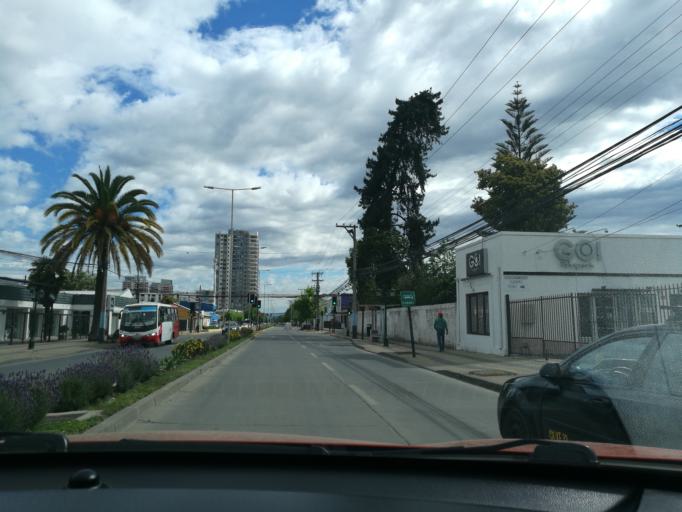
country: CL
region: O'Higgins
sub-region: Provincia de Cachapoal
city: Rancagua
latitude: -34.1741
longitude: -70.7360
